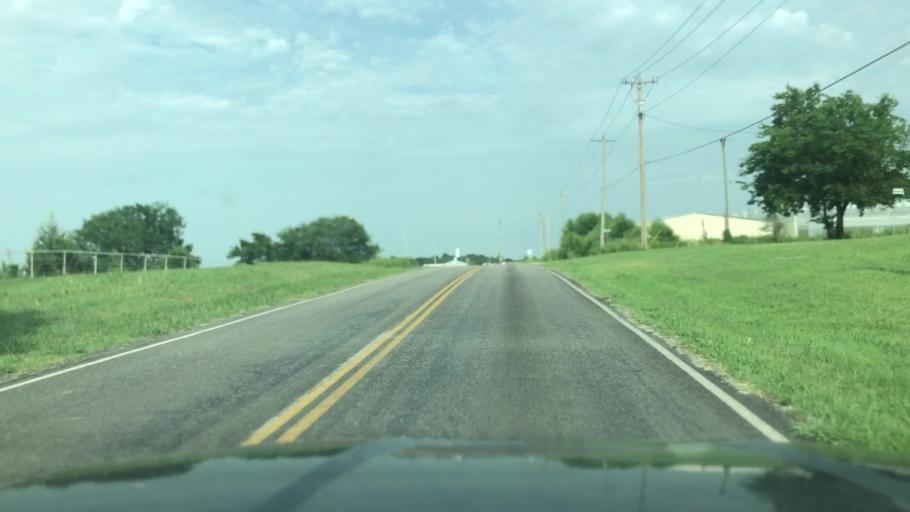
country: US
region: Oklahoma
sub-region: Tulsa County
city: Oakhurst
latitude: 36.0901
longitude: -96.0884
